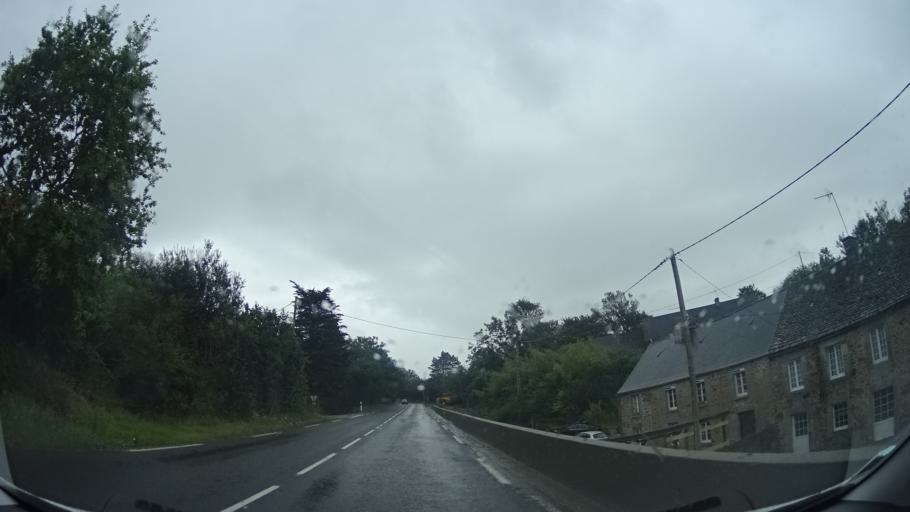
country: FR
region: Lower Normandy
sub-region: Departement de la Manche
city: Beaumont-Hague
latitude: 49.6081
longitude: -1.7910
